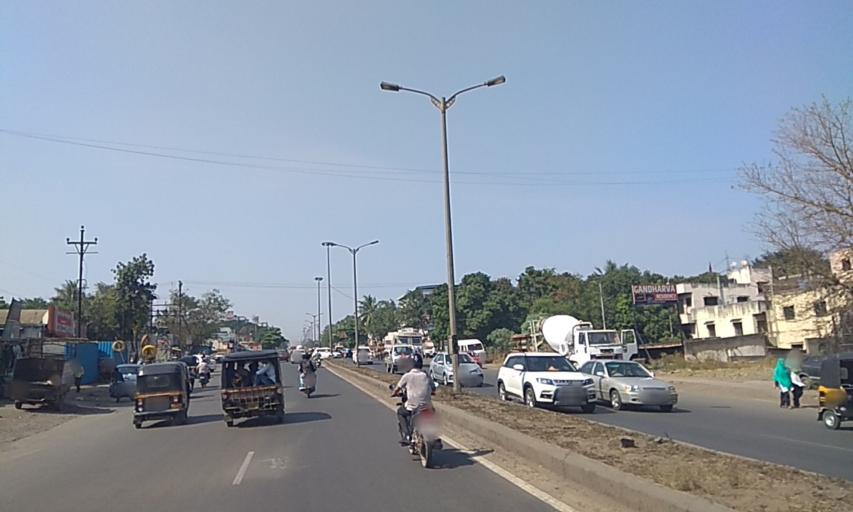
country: IN
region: Maharashtra
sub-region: Pune Division
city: Pune
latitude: 18.4986
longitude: 73.9549
